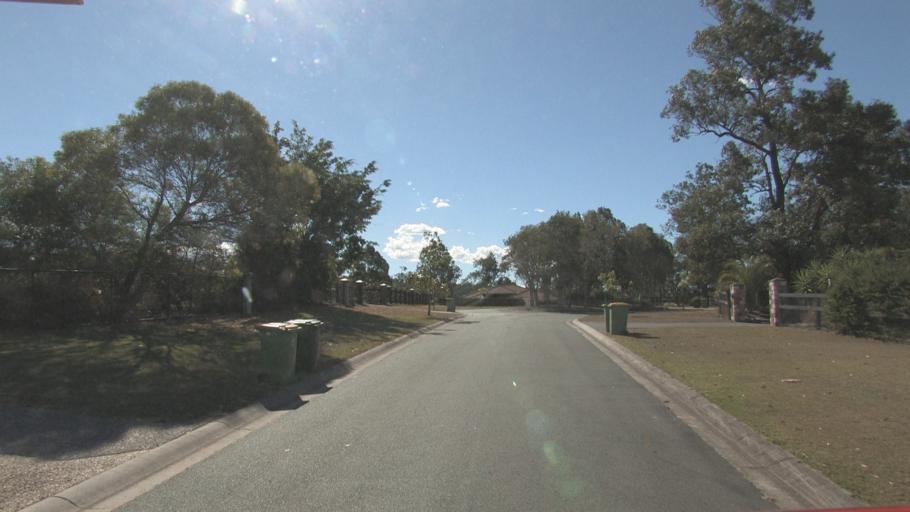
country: AU
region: Queensland
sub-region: Ipswich
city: Springfield Lakes
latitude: -27.7331
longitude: 152.9111
